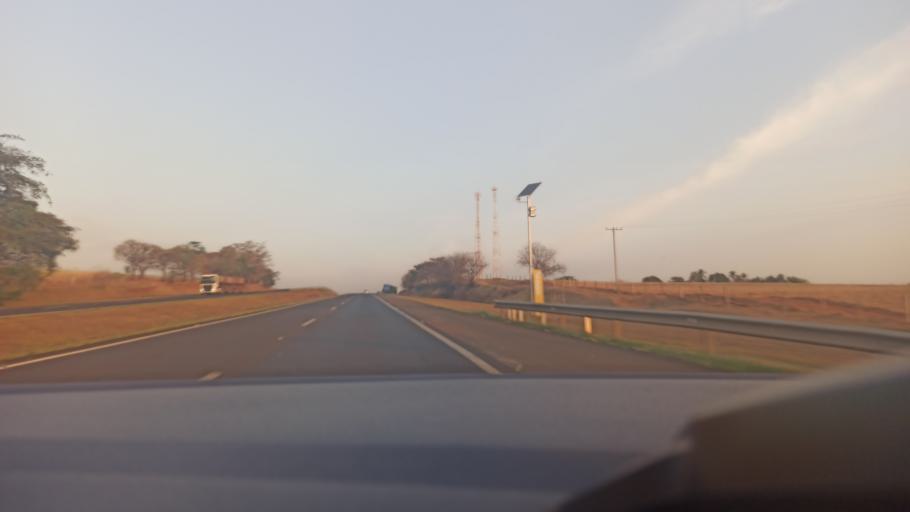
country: BR
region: Sao Paulo
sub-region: Taquaritinga
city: Taquaritinga
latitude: -21.4201
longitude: -48.6791
